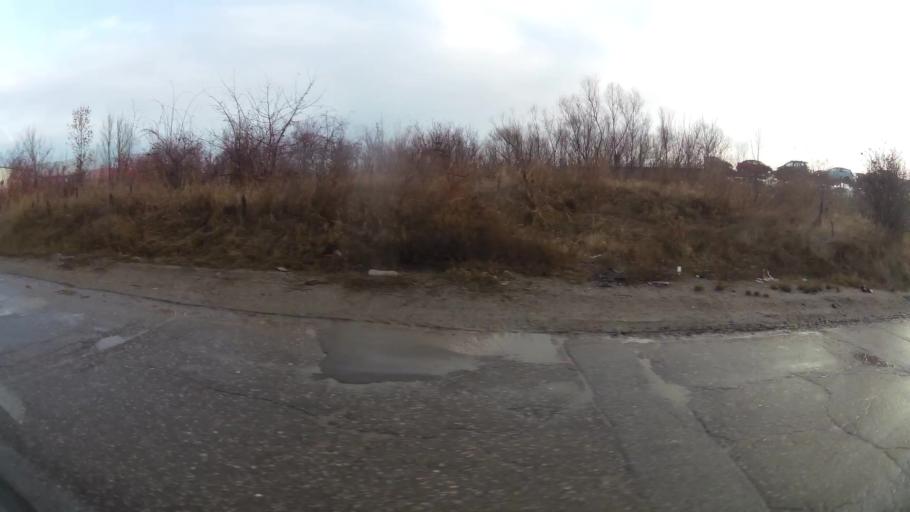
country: BG
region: Sofia-Capital
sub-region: Stolichna Obshtina
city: Sofia
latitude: 42.7403
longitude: 23.3310
